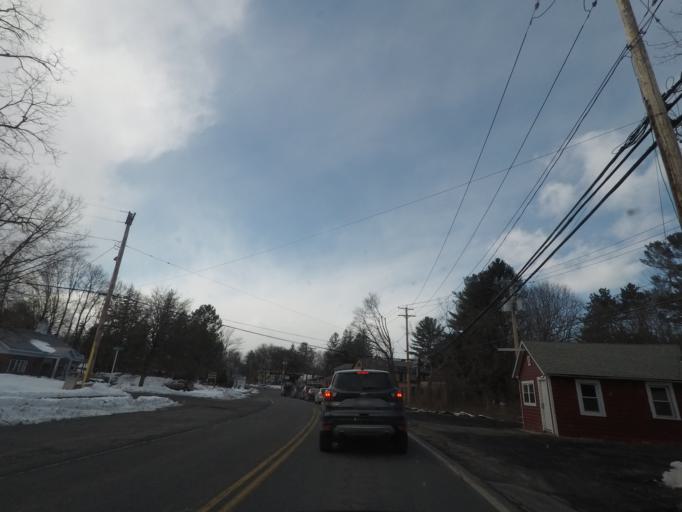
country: US
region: New York
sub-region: Albany County
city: Delmar
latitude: 42.6293
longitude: -73.8642
